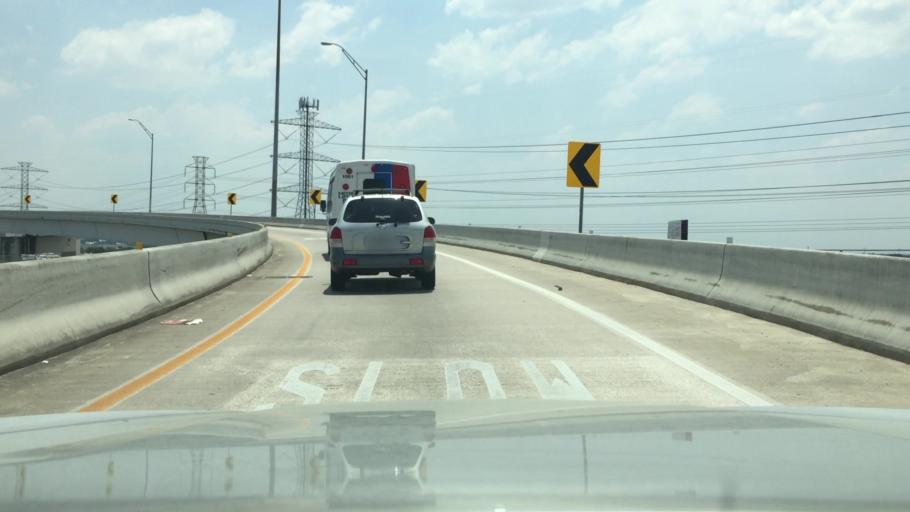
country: US
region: Texas
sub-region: Harris County
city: Bellaire
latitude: 29.7224
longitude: -95.4946
